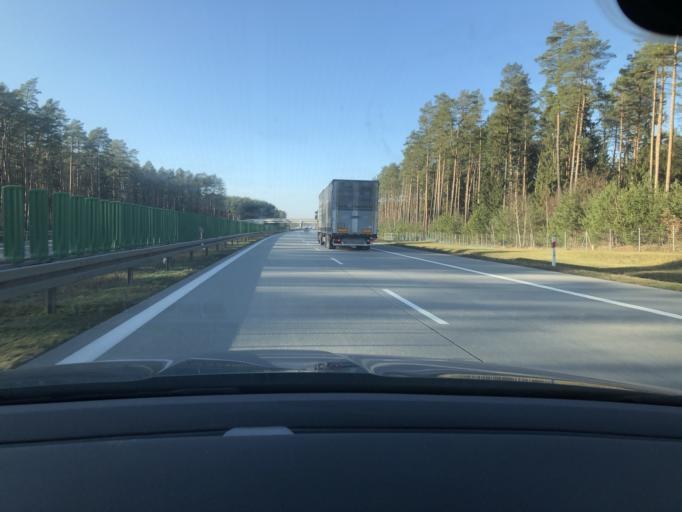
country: PL
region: Lubusz
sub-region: Powiat swiebodzinski
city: Lagow
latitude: 52.3138
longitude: 15.2072
